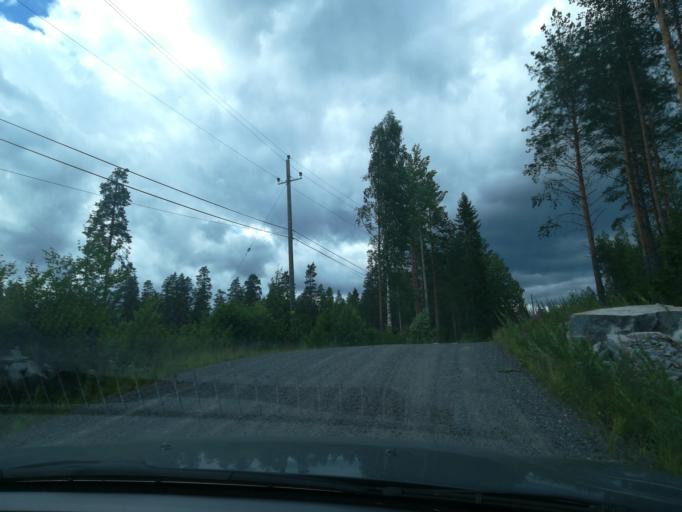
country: FI
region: Southern Savonia
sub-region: Mikkeli
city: Mikkeli
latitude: 61.6614
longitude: 27.1162
